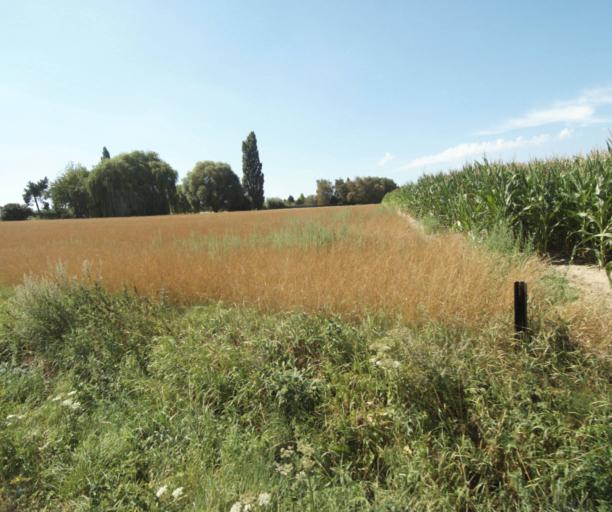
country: FR
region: Nord-Pas-de-Calais
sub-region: Departement du Nord
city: Neuville-en-Ferrain
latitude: 50.7698
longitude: 3.1550
